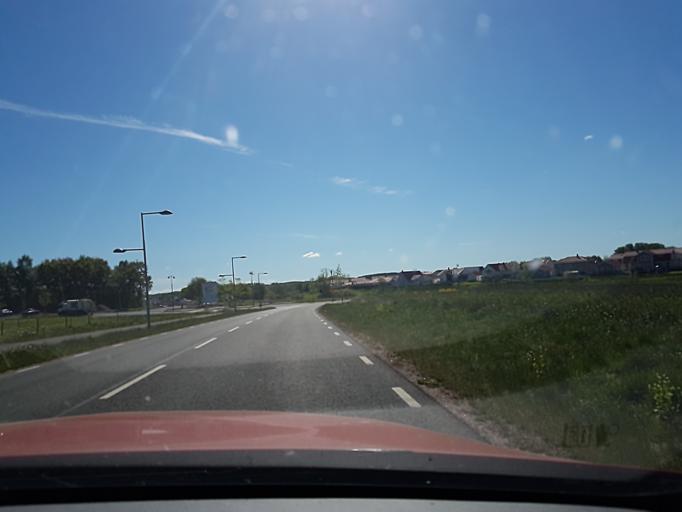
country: SE
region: Vaestra Goetaland
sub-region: Skovde Kommun
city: Skoevde
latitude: 58.4126
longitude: 13.8879
